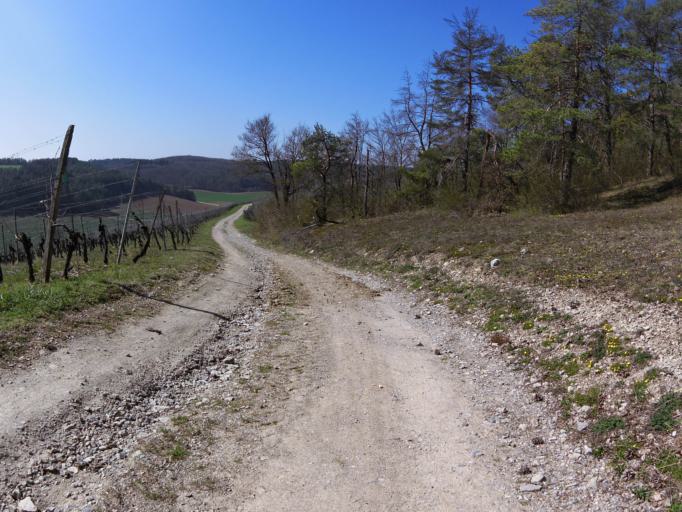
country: DE
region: Bavaria
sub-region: Regierungsbezirk Unterfranken
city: Erlabrunn
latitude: 49.8460
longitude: 9.8189
